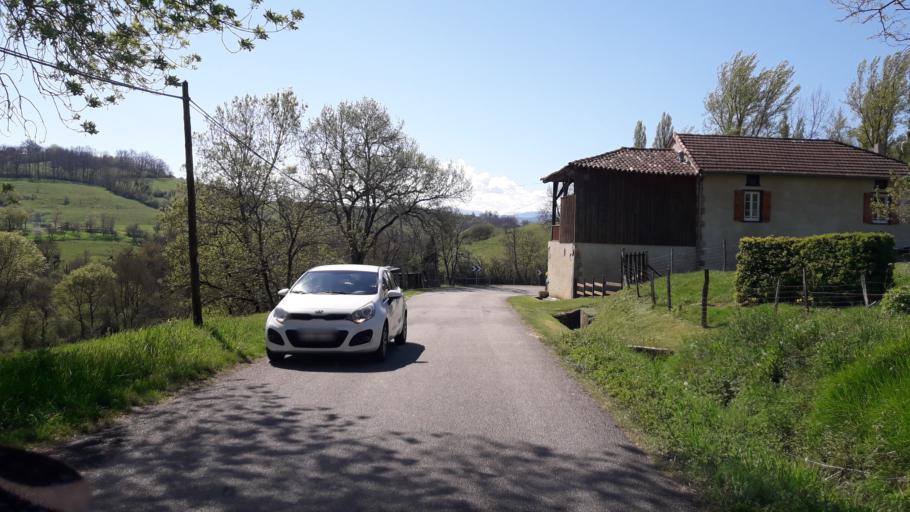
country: FR
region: Midi-Pyrenees
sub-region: Departement de la Haute-Garonne
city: Montesquieu-Volvestre
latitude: 43.1615
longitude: 1.3190
